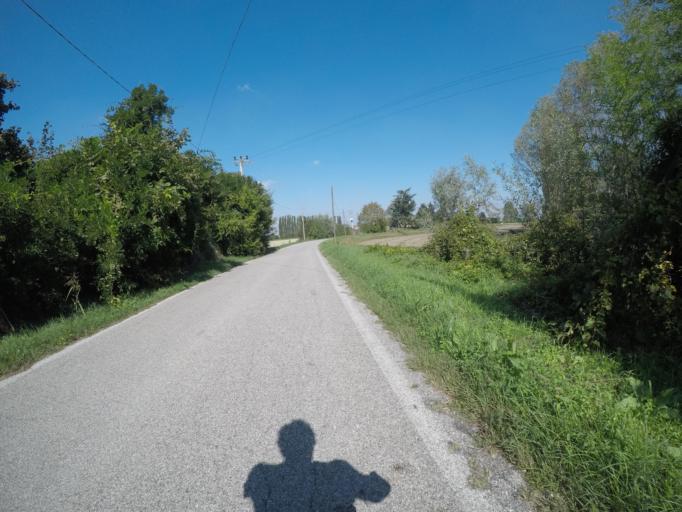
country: IT
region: Veneto
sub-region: Provincia di Rovigo
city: Polesella
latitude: 44.9766
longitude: 11.7548
